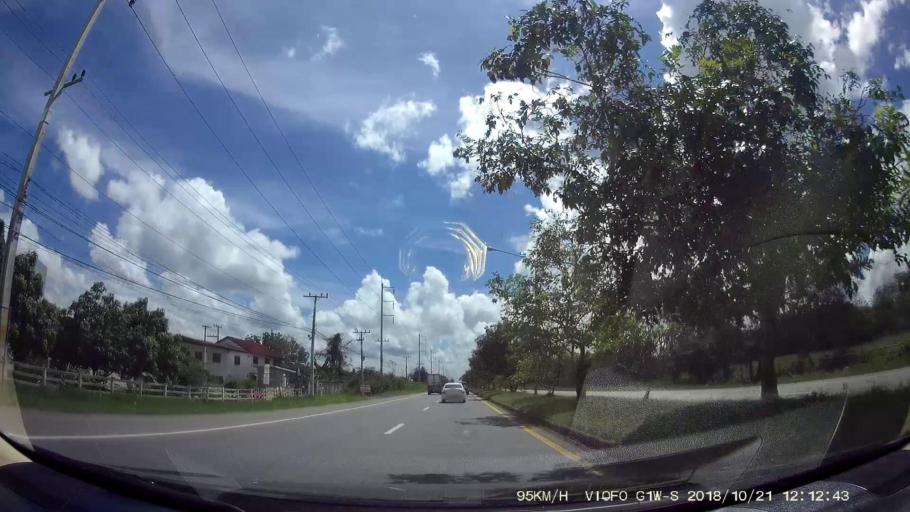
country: TH
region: Chaiyaphum
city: Chatturat
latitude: 15.4034
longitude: 101.8363
